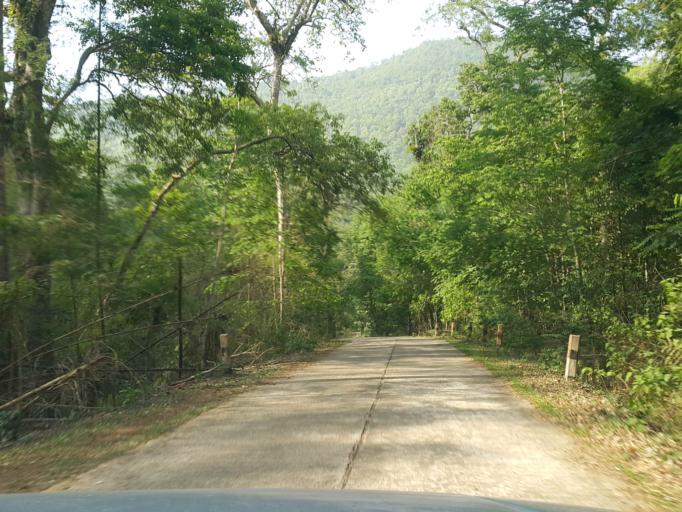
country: TH
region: Chiang Mai
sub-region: Amphoe Chiang Dao
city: Chiang Dao
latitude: 19.3969
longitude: 98.7745
